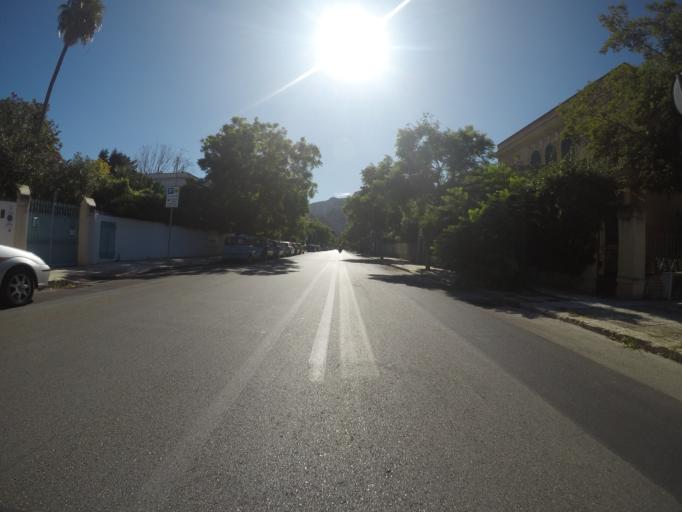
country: IT
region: Sicily
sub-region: Palermo
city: Palermo
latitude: 38.1994
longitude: 13.3274
